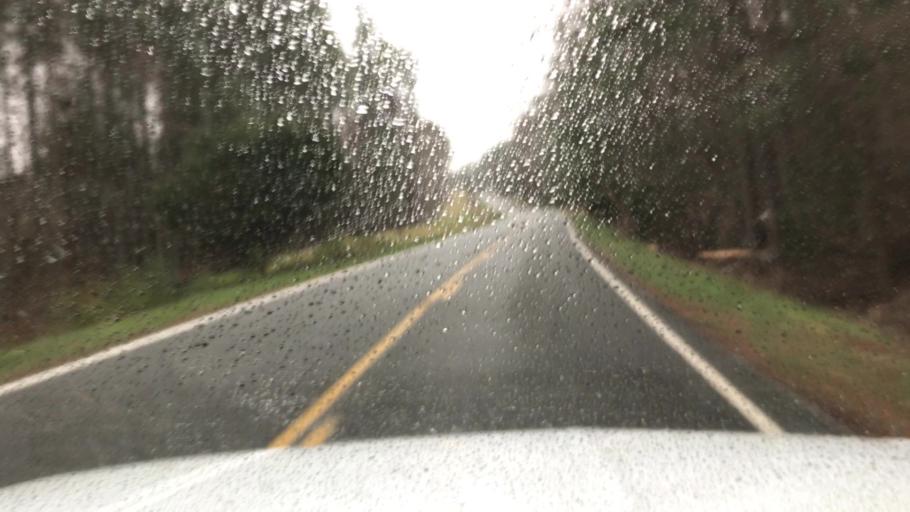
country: US
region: Virginia
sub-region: Henrico County
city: Short Pump
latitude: 37.6480
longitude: -77.6782
